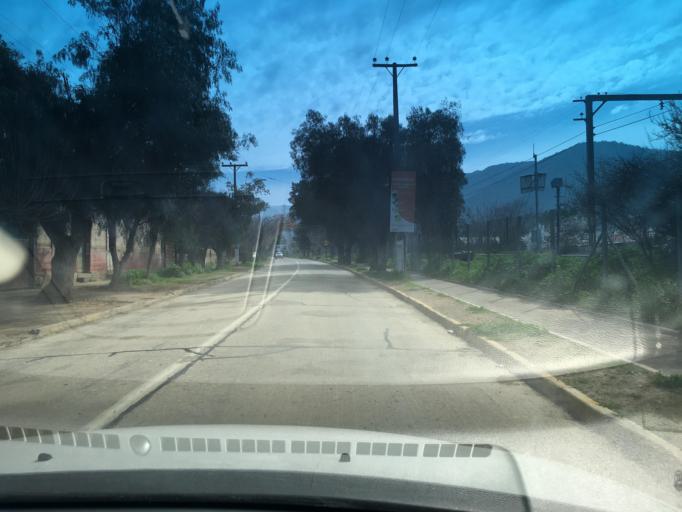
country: CL
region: Santiago Metropolitan
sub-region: Provincia de Chacabuco
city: Lampa
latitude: -33.0777
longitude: -70.9275
